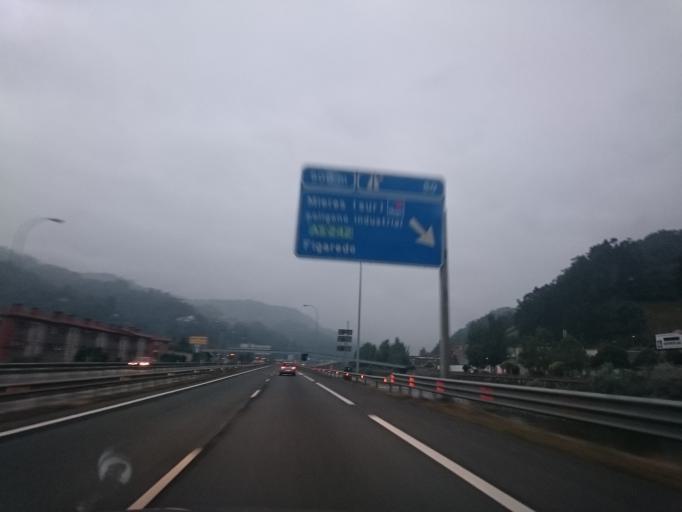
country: ES
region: Asturias
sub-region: Province of Asturias
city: Mieres
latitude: 43.2463
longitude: -5.7805
